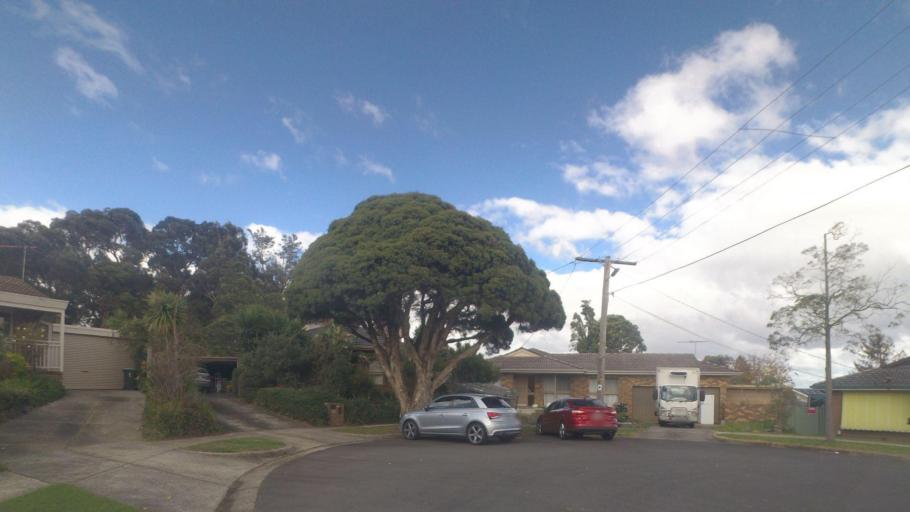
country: AU
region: Victoria
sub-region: Whitehorse
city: Vermont South
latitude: -37.8519
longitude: 145.1782
